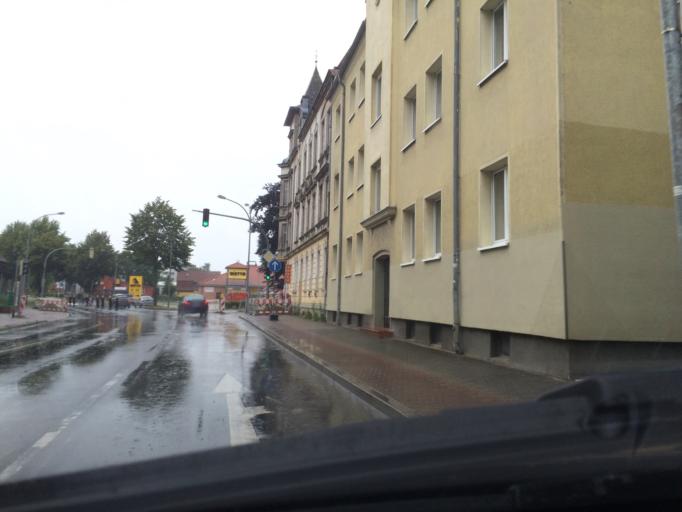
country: DE
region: Mecklenburg-Vorpommern
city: Stralsund
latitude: 54.3224
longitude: 13.0792
